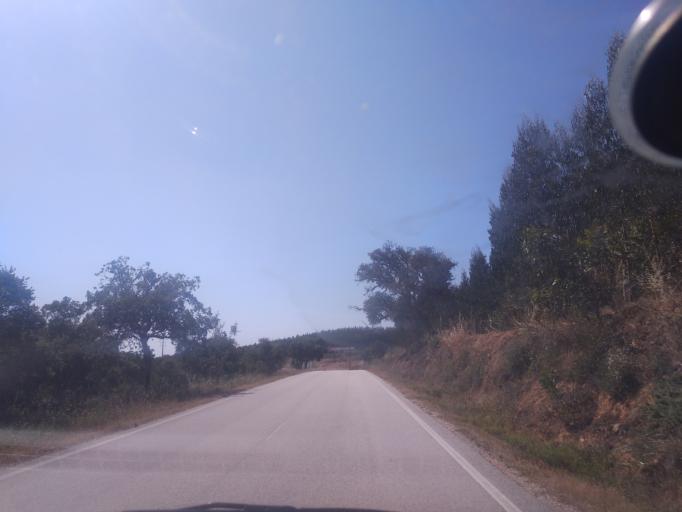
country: PT
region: Faro
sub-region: Aljezur
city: Aljezur
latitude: 37.2178
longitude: -8.7900
